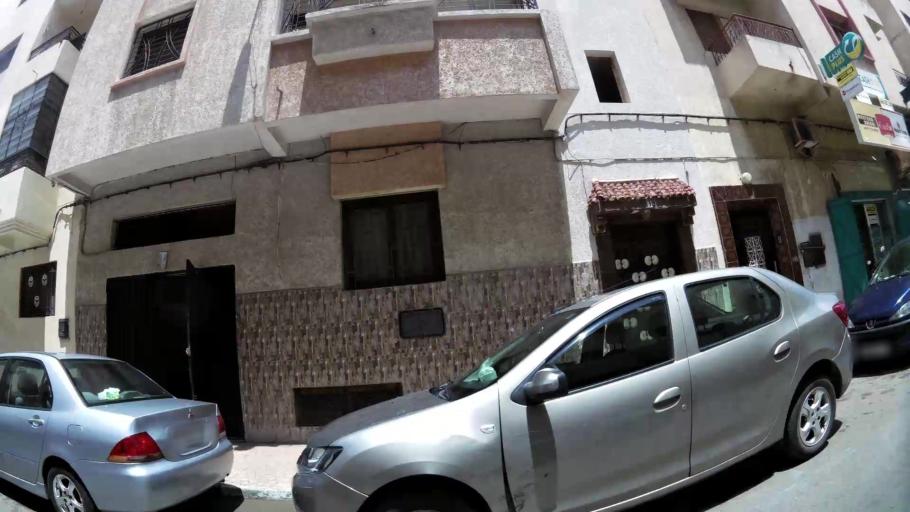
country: MA
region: Rabat-Sale-Zemmour-Zaer
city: Sale
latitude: 34.0425
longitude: -6.8208
